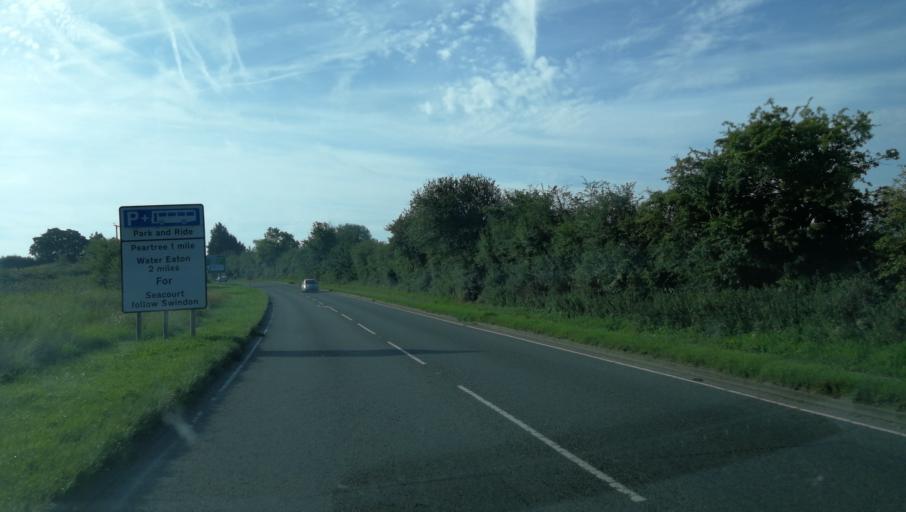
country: GB
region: England
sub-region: Oxfordshire
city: Yarnton
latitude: 51.7991
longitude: -1.2899
